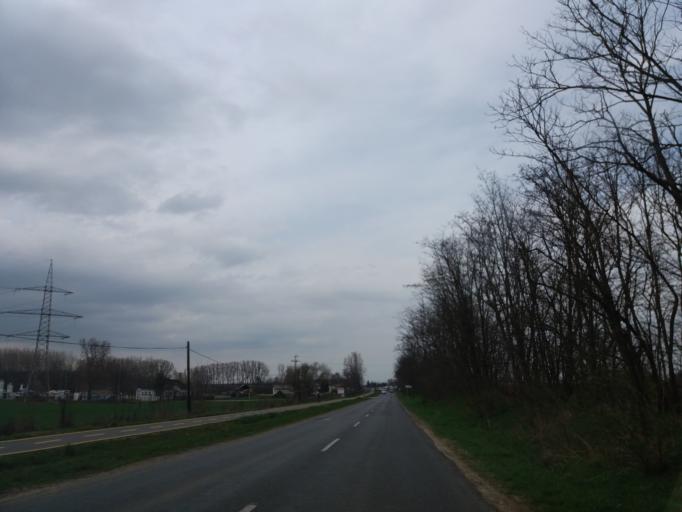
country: HU
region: Szabolcs-Szatmar-Bereg
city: Anarcs
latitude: 48.1949
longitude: 22.0971
